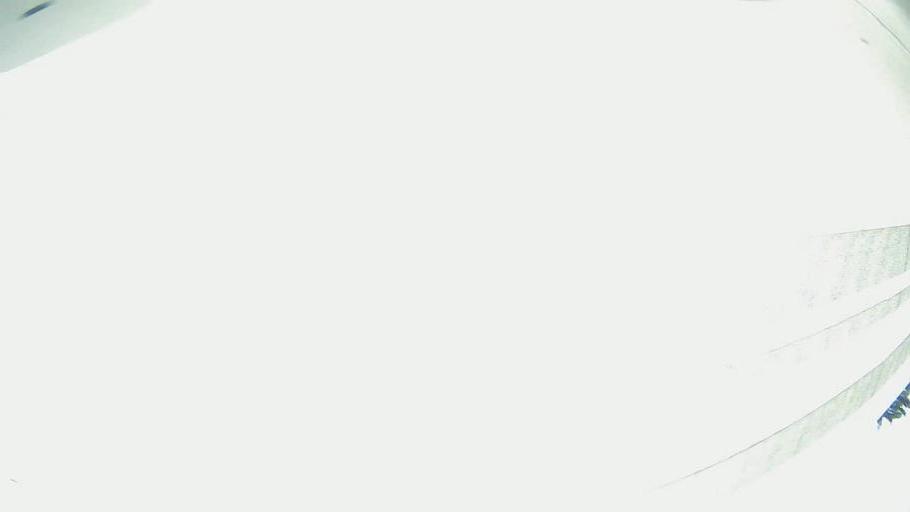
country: US
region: Michigan
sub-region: Oakland County
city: Oak Park
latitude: 42.4775
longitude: -83.1974
